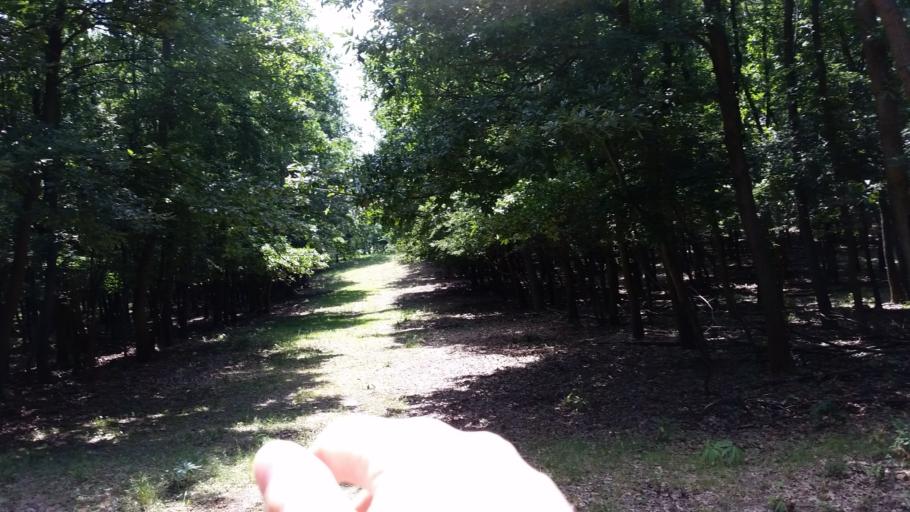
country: HU
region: Komarom-Esztergom
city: Bajna
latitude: 47.5906
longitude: 18.5932
